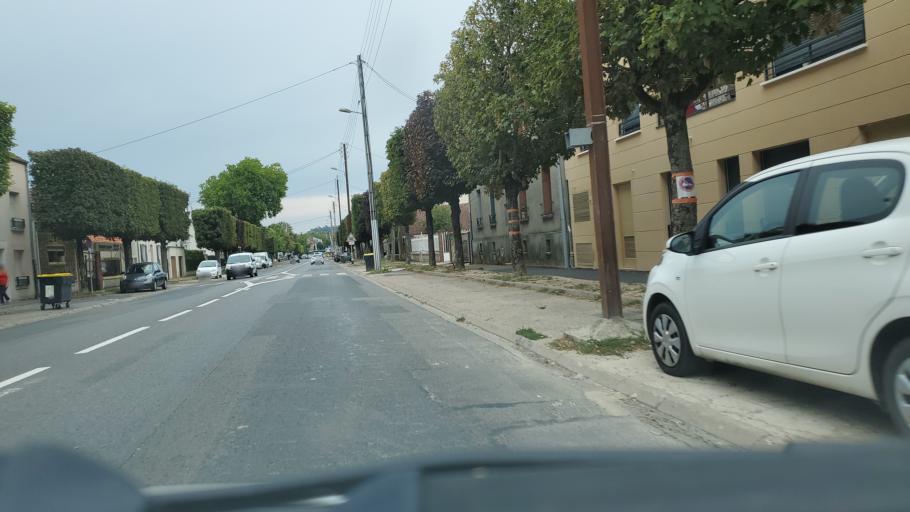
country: FR
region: Ile-de-France
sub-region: Departement de Seine-et-Marne
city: Coulommiers
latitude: 48.8052
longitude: 3.0847
